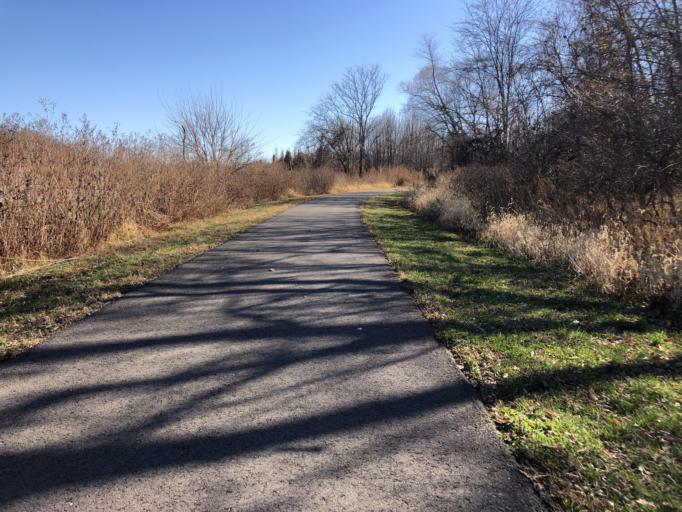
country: US
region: Kansas
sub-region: Johnson County
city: Gardner
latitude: 38.8825
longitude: -94.9720
